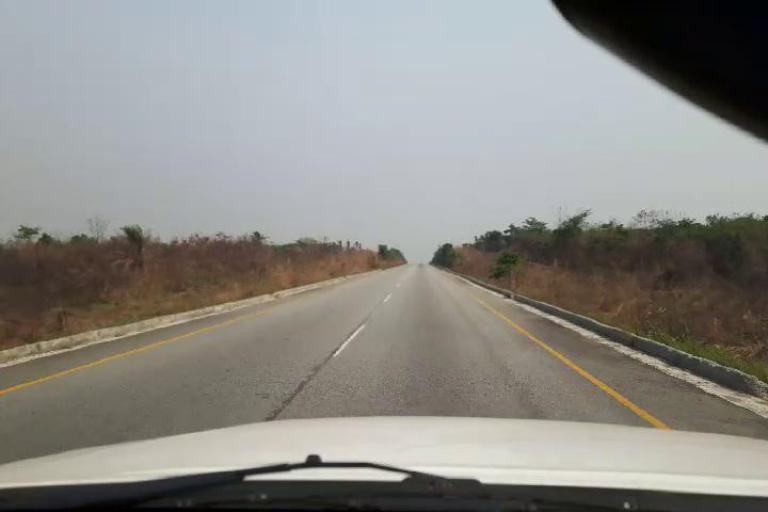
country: SL
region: Southern Province
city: Largo
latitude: 8.2311
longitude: -12.0797
